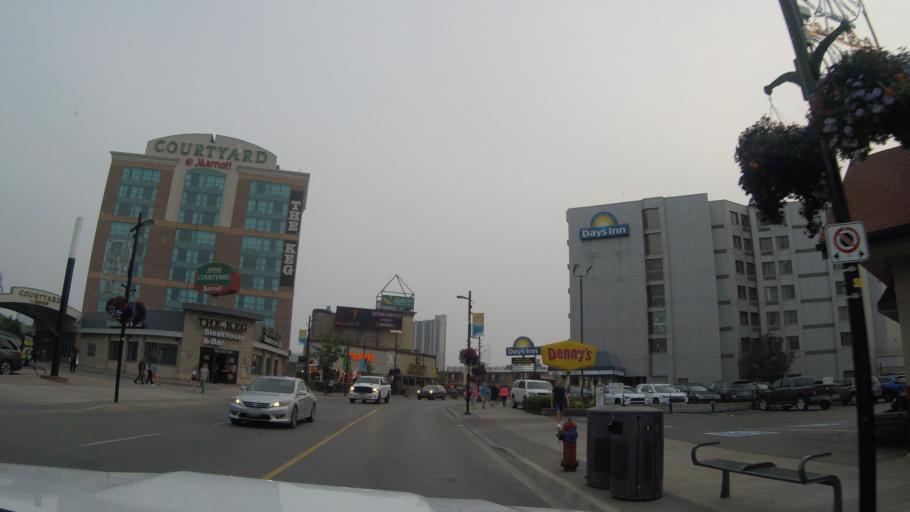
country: CA
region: Ontario
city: Niagara Falls
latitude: 43.0899
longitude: -79.0796
